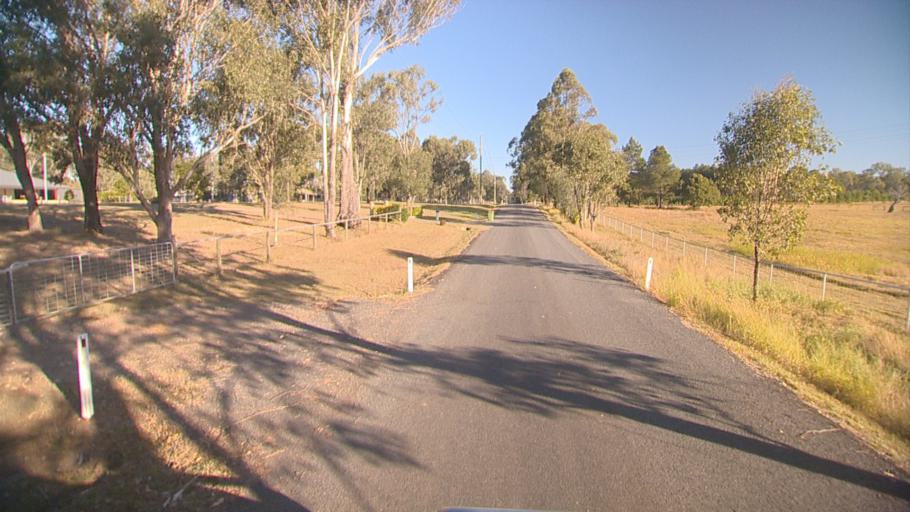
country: AU
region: Queensland
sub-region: Logan
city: North Maclean
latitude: -27.7765
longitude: 153.0473
